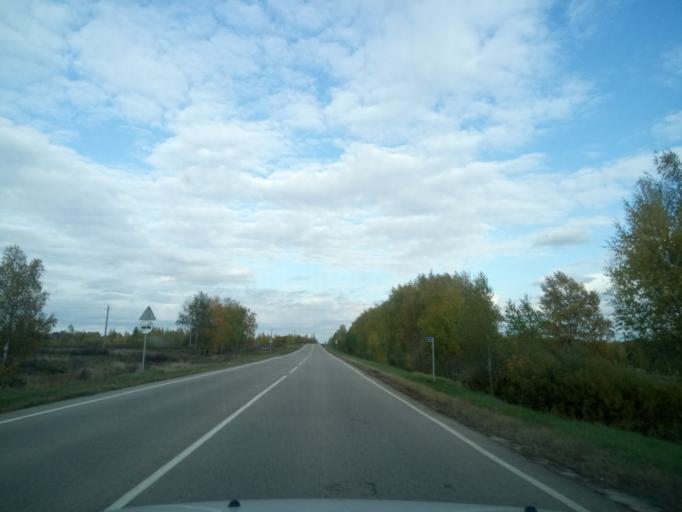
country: RU
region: Nizjnij Novgorod
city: Bol'shoye Boldino
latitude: 54.9212
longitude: 45.1386
